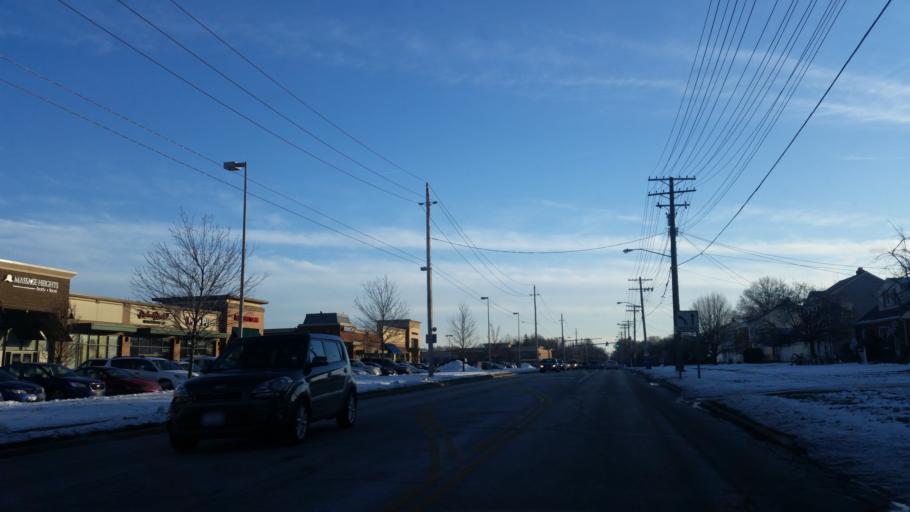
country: US
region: Ohio
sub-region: Cuyahoga County
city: Rocky River
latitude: 41.4609
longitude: -81.8528
